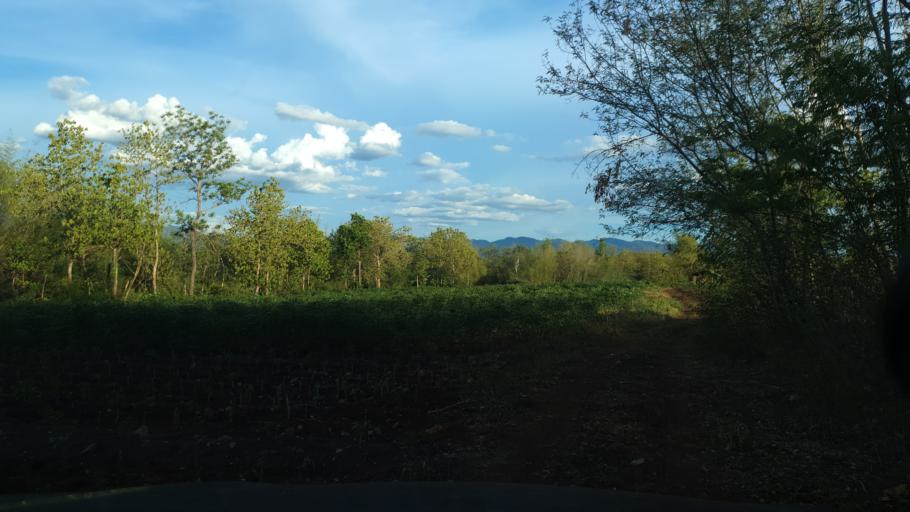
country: TH
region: Lampang
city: Sop Prap
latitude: 17.9626
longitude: 99.3520
